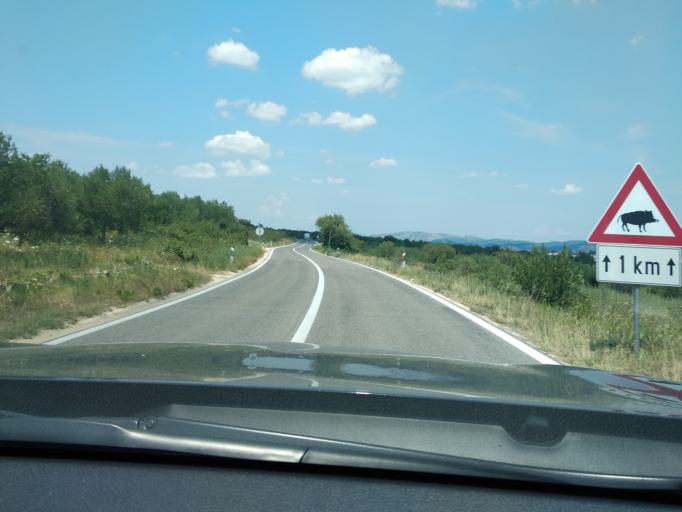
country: HR
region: Sibensko-Kniniska
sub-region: Grad Sibenik
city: Pirovac
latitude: 43.8016
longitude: 15.6742
